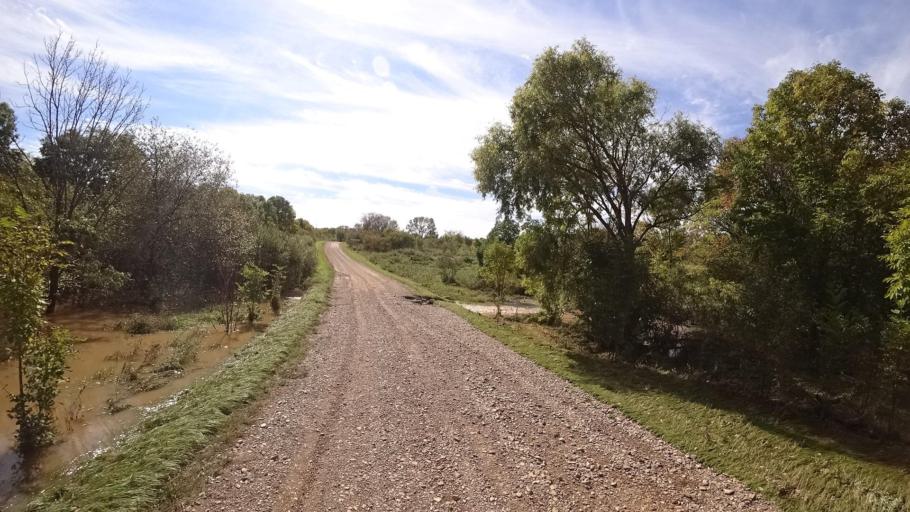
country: RU
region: Primorskiy
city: Kirovskiy
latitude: 44.7614
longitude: 133.6108
